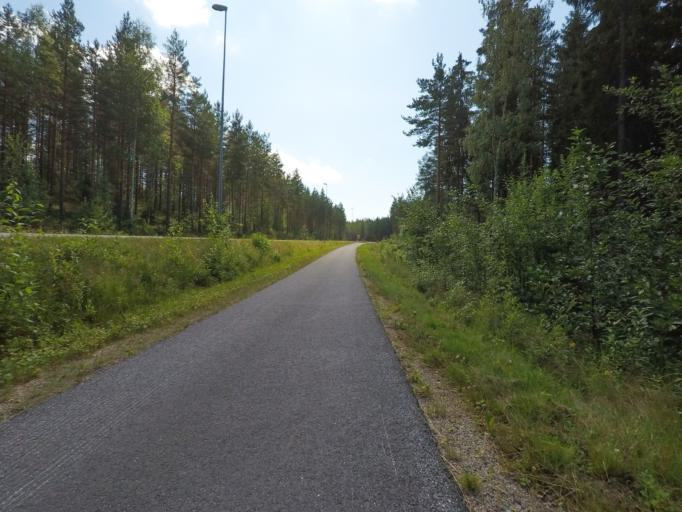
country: FI
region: Southern Savonia
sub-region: Mikkeli
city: Puumala
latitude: 61.5122
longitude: 28.1646
